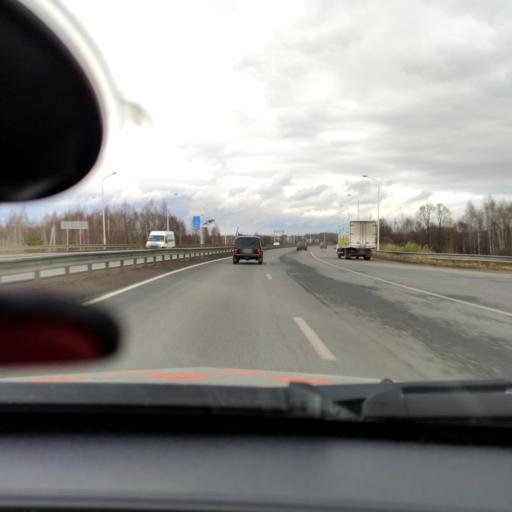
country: RU
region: Bashkortostan
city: Ufa
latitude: 54.6642
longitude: 56.0741
